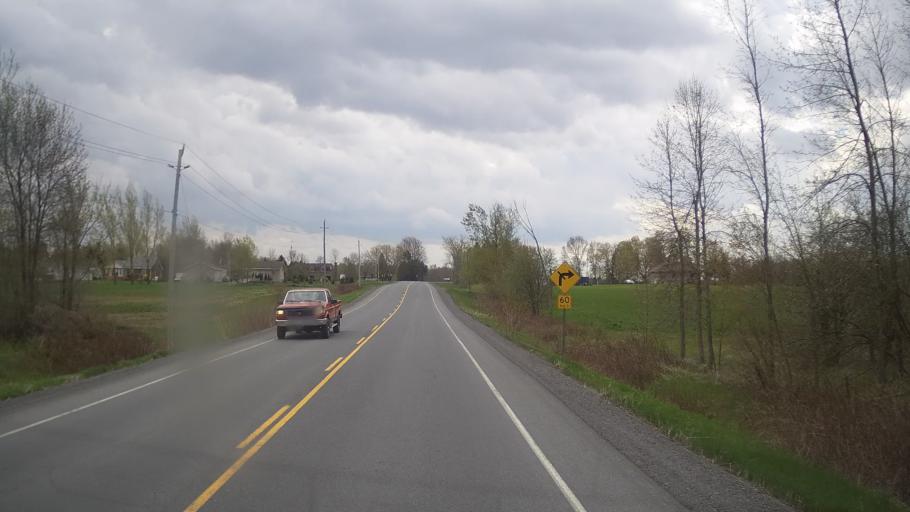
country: CA
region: Ontario
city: Hawkesbury
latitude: 45.5678
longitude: -74.5256
